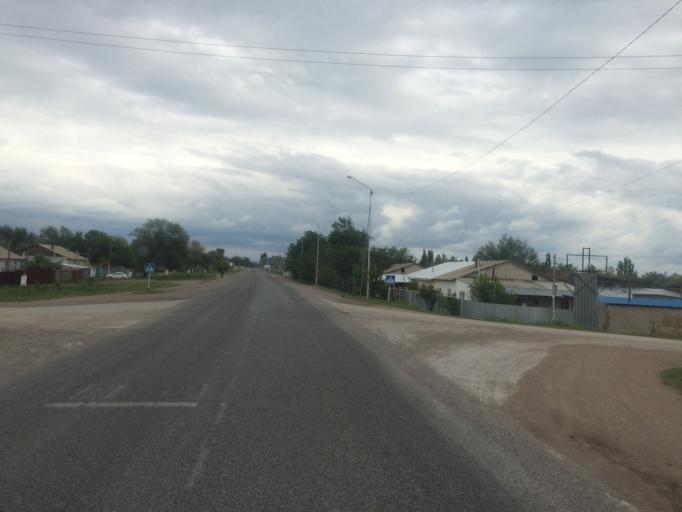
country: KZ
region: Zhambyl
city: Georgiyevka
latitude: 43.2280
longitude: 74.3864
